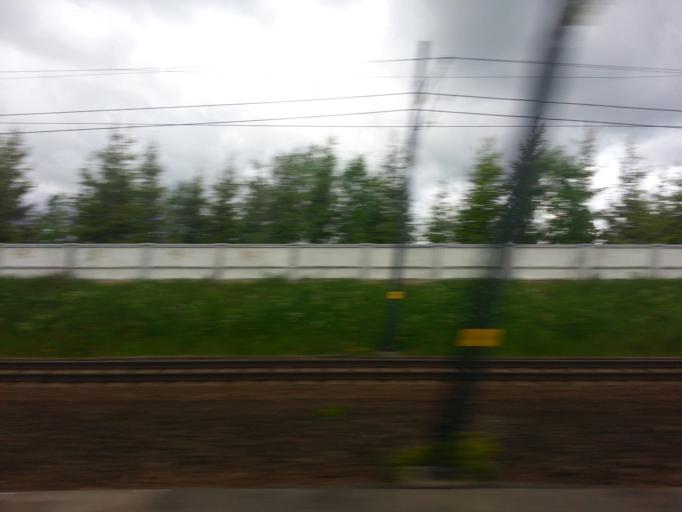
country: NO
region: Akershus
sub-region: Ullensaker
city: Klofta
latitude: 60.0913
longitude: 11.1405
